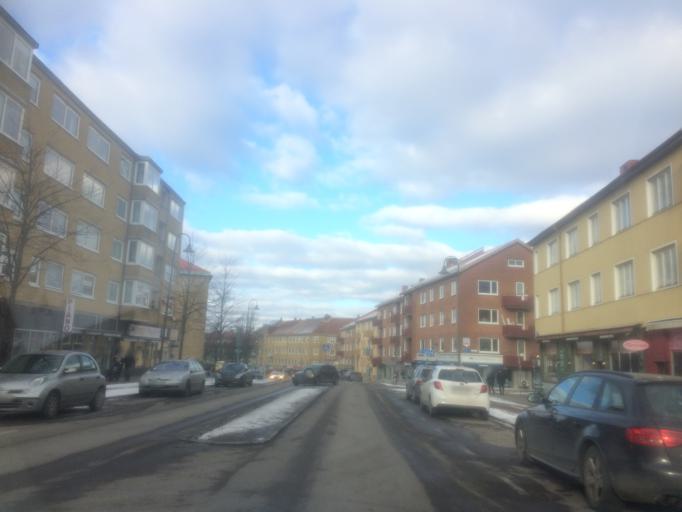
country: SE
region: Vaestra Goetaland
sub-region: Goteborg
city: Goeteborg
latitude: 57.7117
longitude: 12.0073
